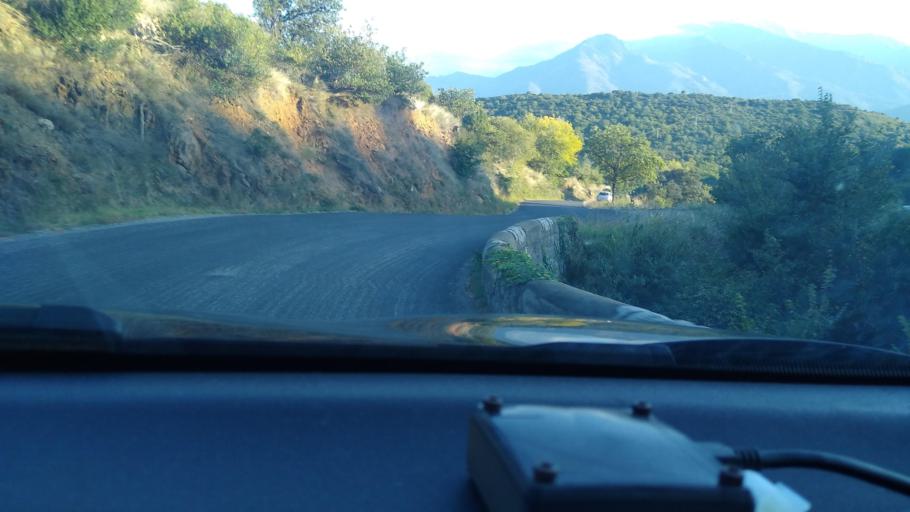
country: FR
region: Languedoc-Roussillon
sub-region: Departement des Pyrenees-Orientales
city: Ria-Sirach
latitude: 42.6366
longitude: 2.4156
